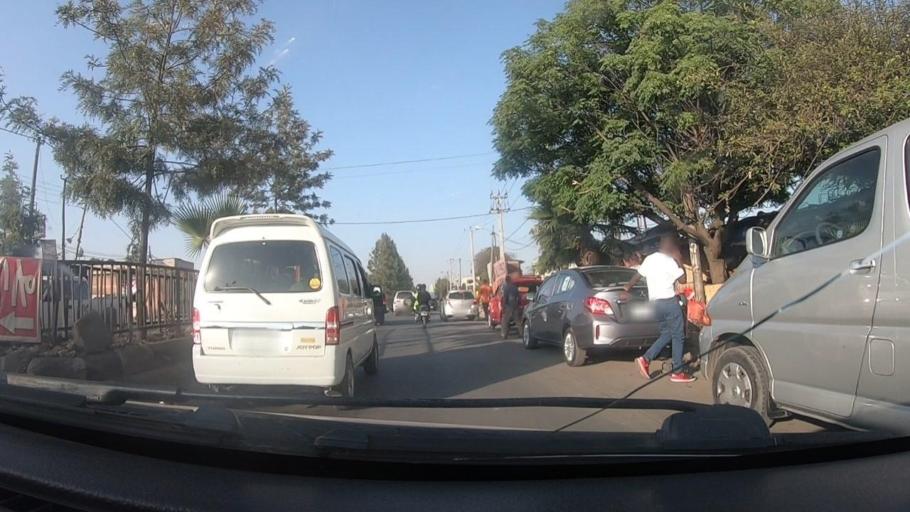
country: ET
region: Adis Abeba
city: Addis Ababa
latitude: 8.9930
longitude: 38.7531
